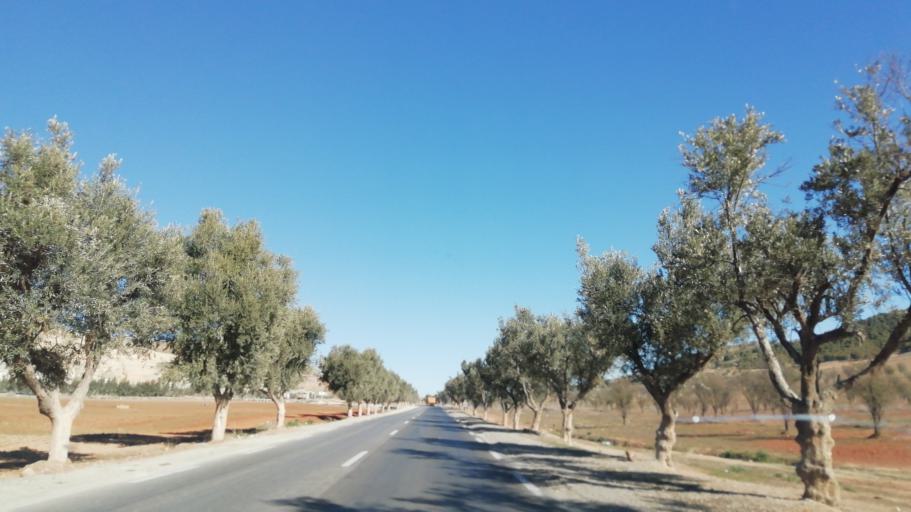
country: DZ
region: Mascara
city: Mascara
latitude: 35.2369
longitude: 0.1170
